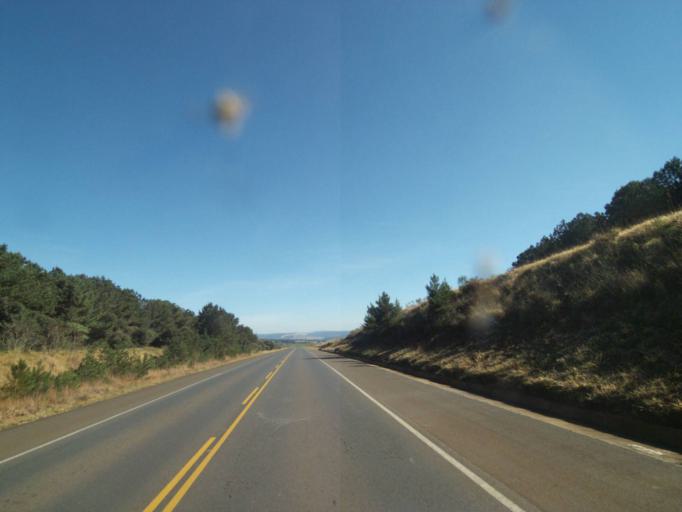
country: BR
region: Parana
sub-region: Tibagi
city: Tibagi
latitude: -24.4349
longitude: -50.4175
